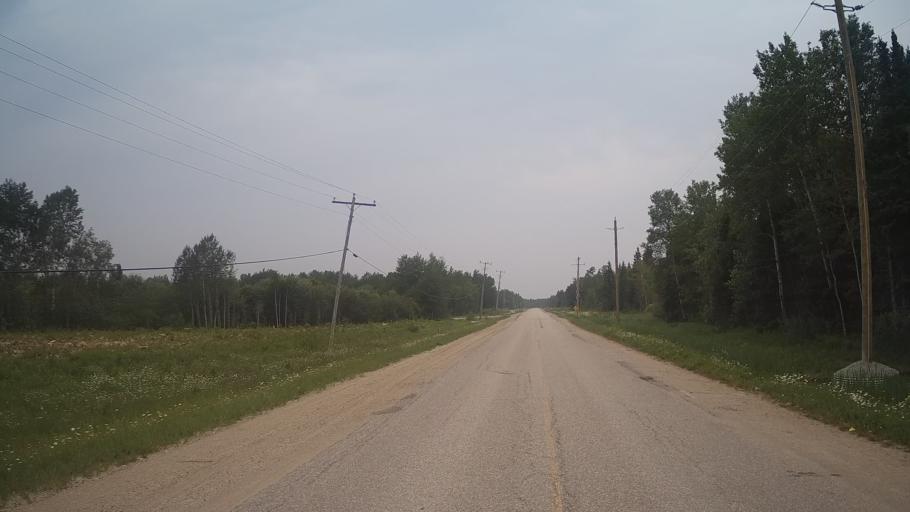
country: CA
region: Ontario
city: Hearst
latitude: 49.7459
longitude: -84.1279
